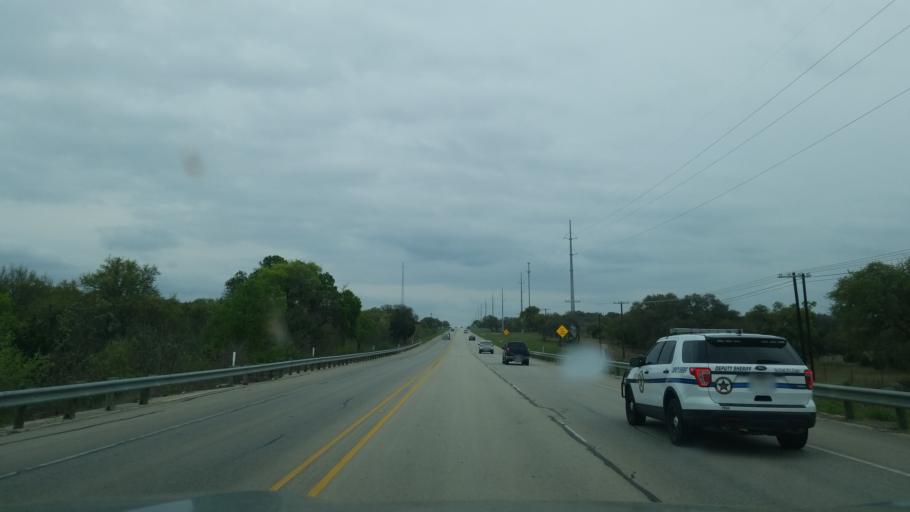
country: US
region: Texas
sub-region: Blanco County
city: Blanco
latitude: 30.0555
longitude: -98.4106
